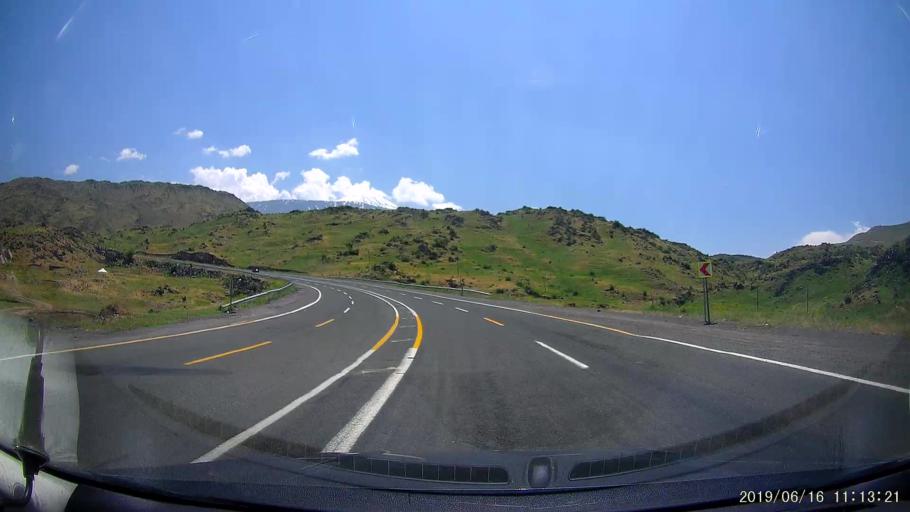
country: TR
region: Igdir
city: Igdir
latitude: 39.7848
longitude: 44.1363
